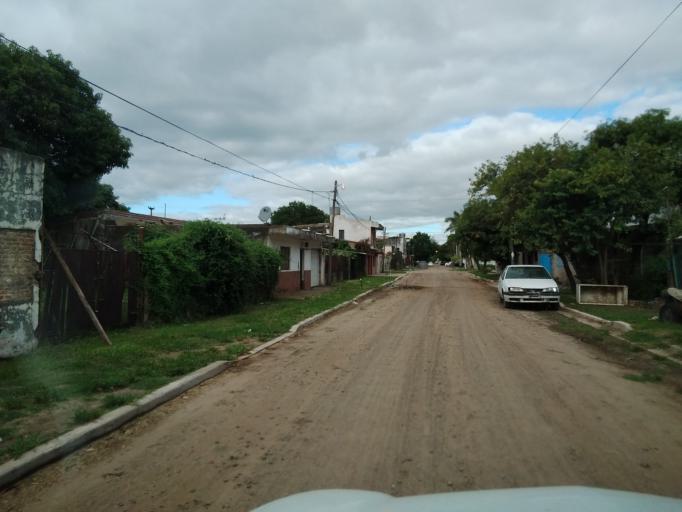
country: AR
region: Corrientes
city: Corrientes
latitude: -27.4749
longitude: -58.8112
